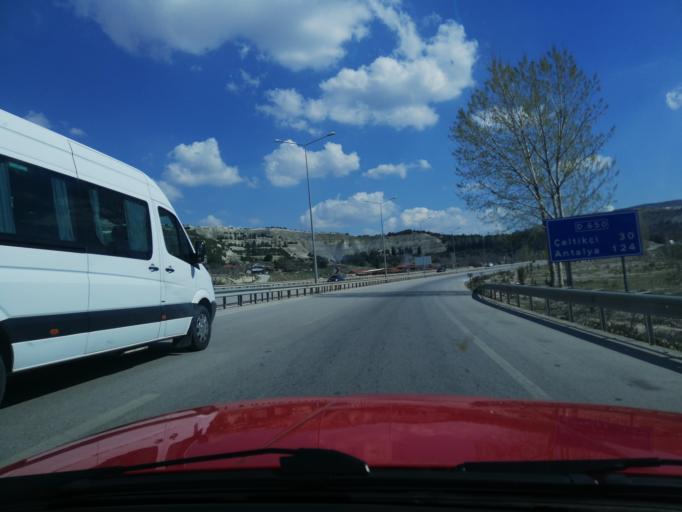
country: TR
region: Burdur
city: Burdur
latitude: 37.7083
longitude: 30.3040
